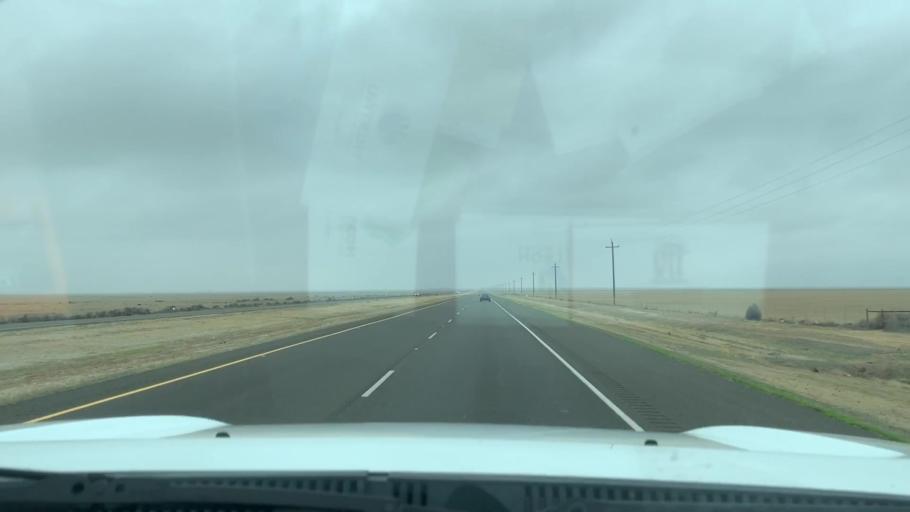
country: US
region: California
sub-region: Kern County
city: Lost Hills
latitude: 35.6158
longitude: -119.7895
